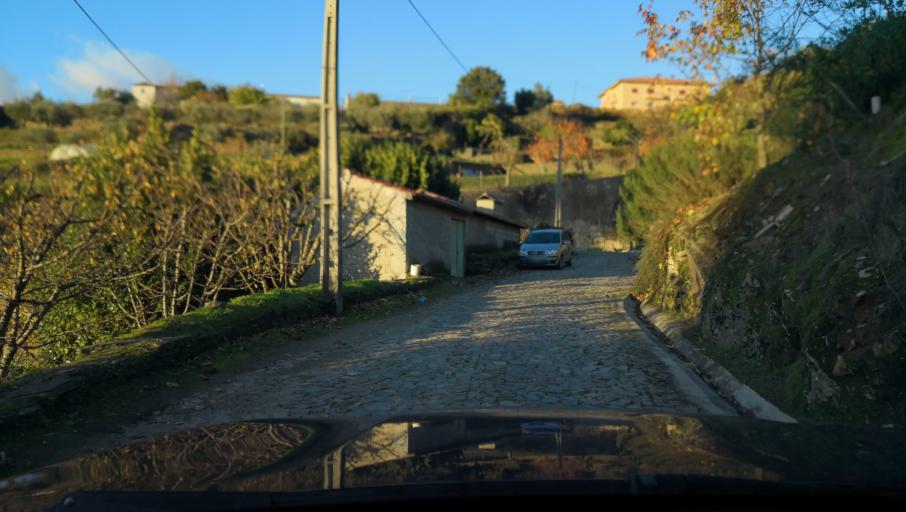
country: PT
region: Vila Real
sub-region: Vila Real
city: Vila Real
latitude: 41.2788
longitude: -7.7385
